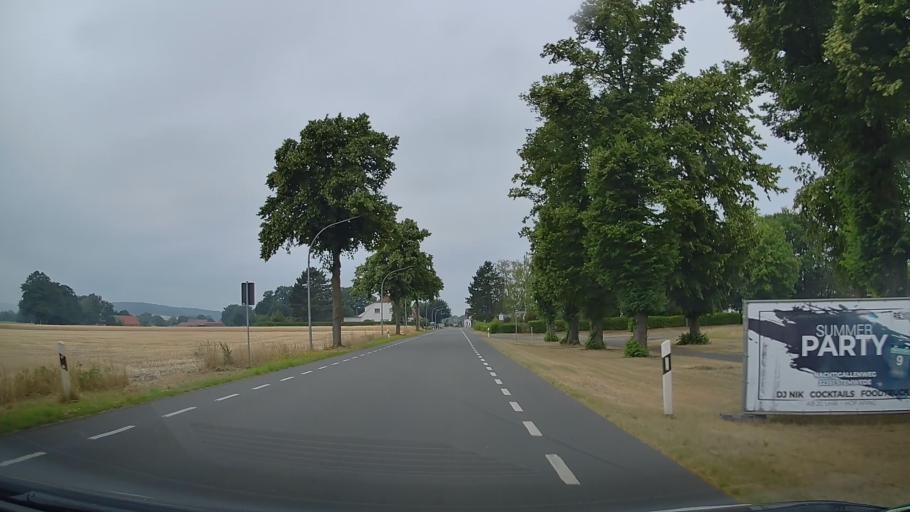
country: DE
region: Lower Saxony
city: Brockum
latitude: 52.4638
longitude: 8.5087
